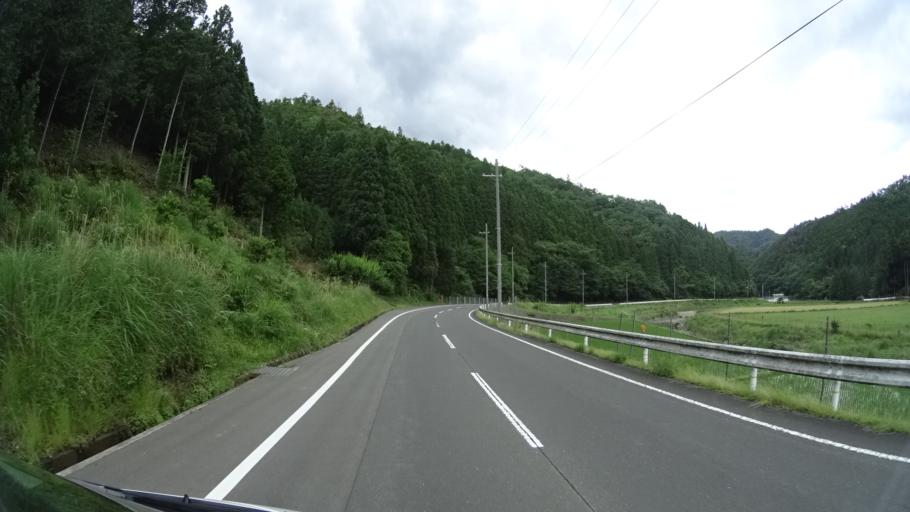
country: JP
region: Hyogo
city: Sasayama
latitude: 35.0573
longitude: 135.3928
